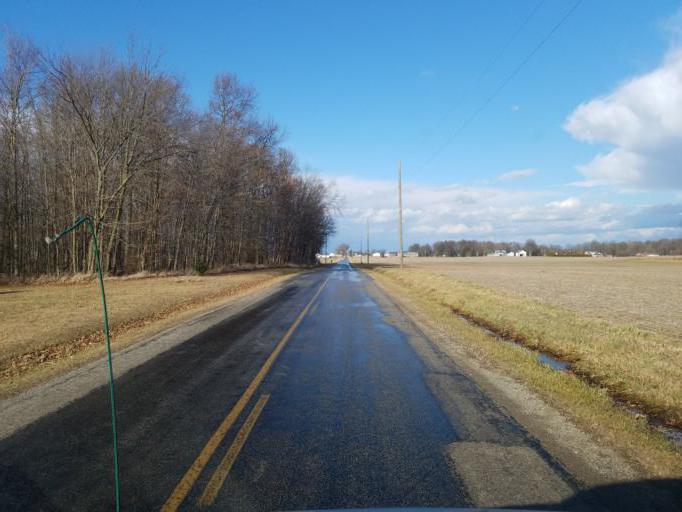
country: US
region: Ohio
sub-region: Marion County
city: Prospect
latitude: 40.4839
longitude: -83.1317
